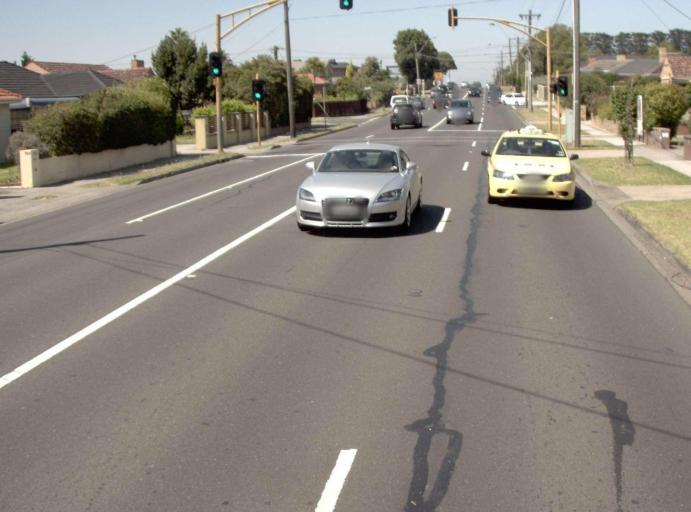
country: AU
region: Victoria
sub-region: Monash
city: Oakleigh South
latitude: -37.9192
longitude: 145.0833
